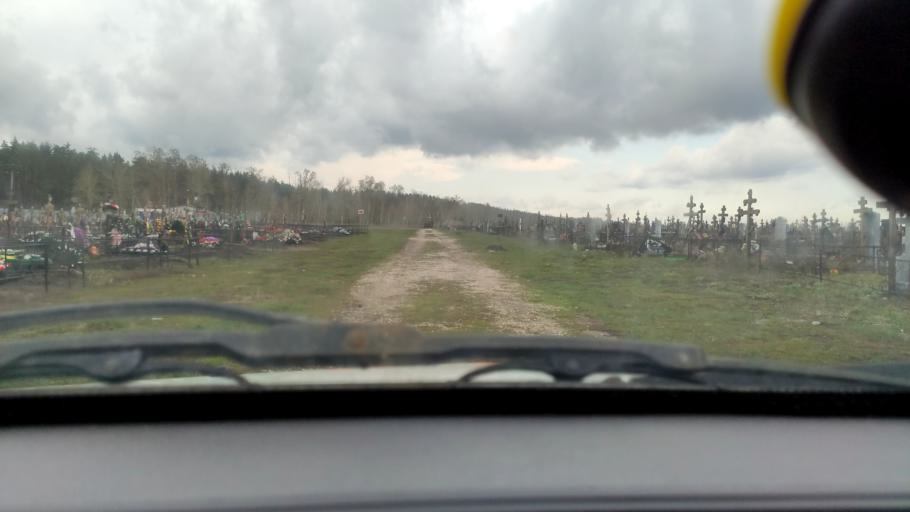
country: RU
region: Samara
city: Povolzhskiy
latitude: 53.6317
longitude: 49.6582
